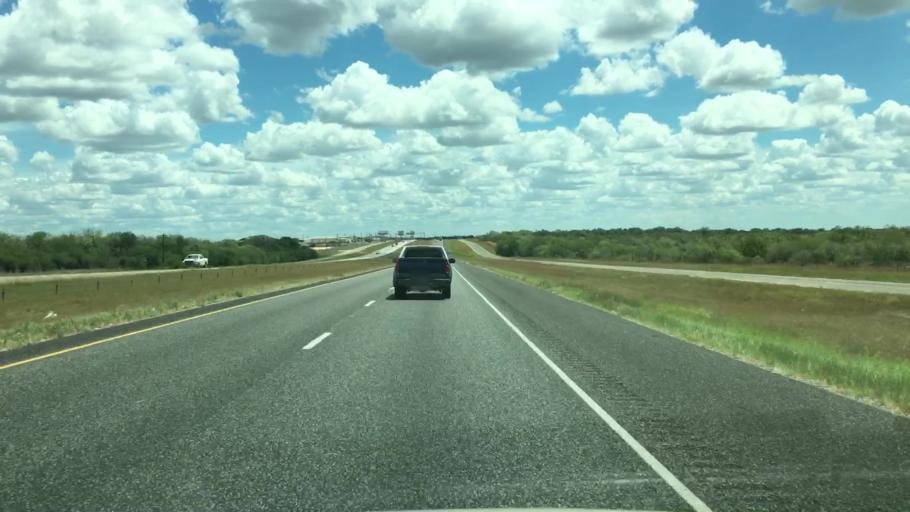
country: US
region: Texas
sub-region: Atascosa County
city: Pleasanton
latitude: 28.8980
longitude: -98.4178
